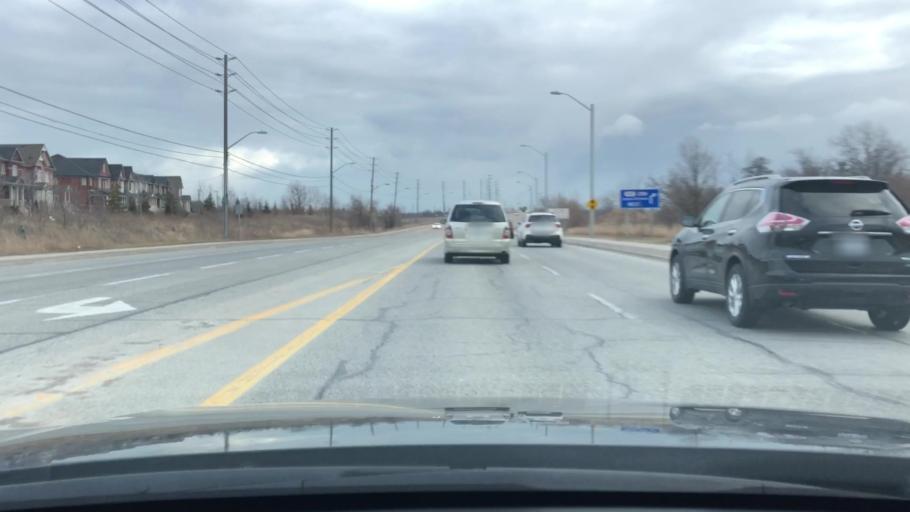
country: CA
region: Ontario
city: Markham
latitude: 43.8752
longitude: -79.2340
